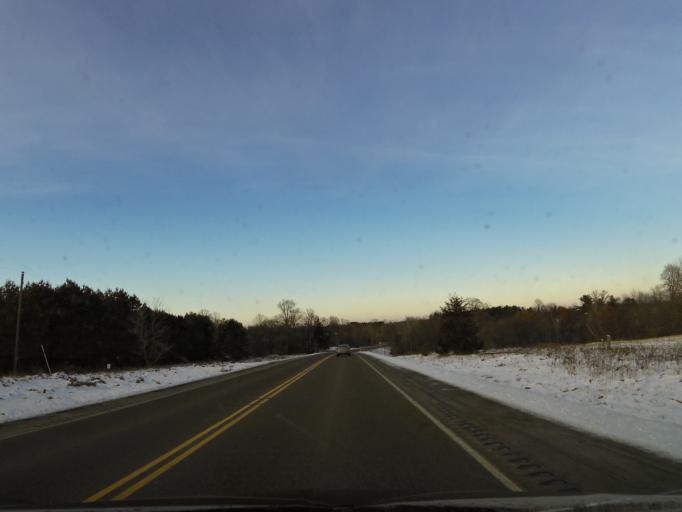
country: US
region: Wisconsin
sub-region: Polk County
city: Osceola
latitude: 45.3394
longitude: -92.7240
